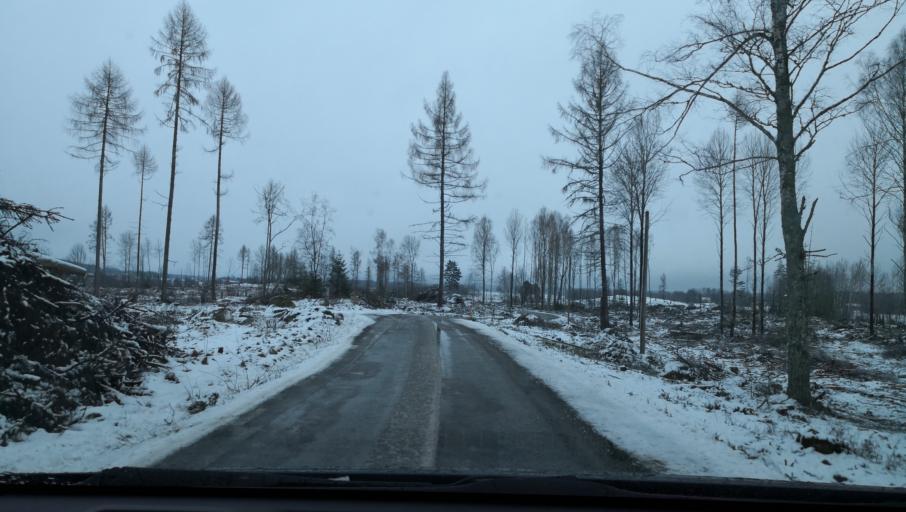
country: SE
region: Vaestmanland
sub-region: Kopings Kommun
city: Kolsva
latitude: 59.5461
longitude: 15.8804
